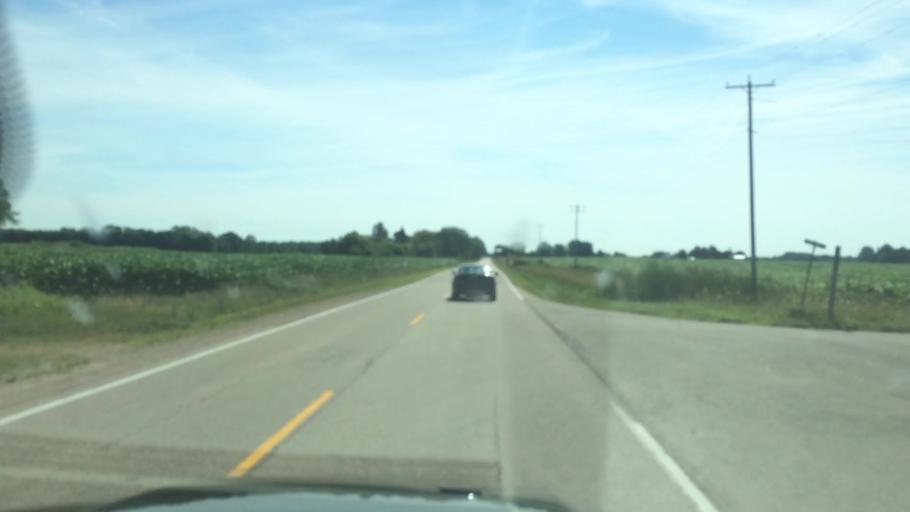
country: US
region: Wisconsin
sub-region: Oconto County
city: Gillett
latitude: 44.7873
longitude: -88.3429
